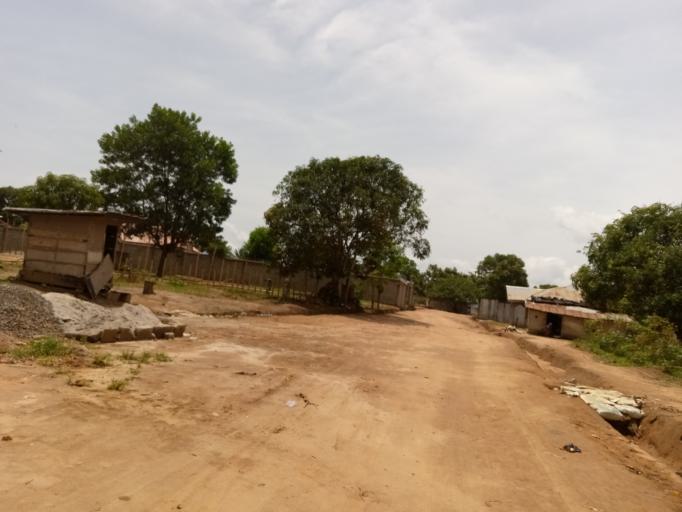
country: SL
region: Western Area
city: Waterloo
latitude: 8.3273
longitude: -13.0435
